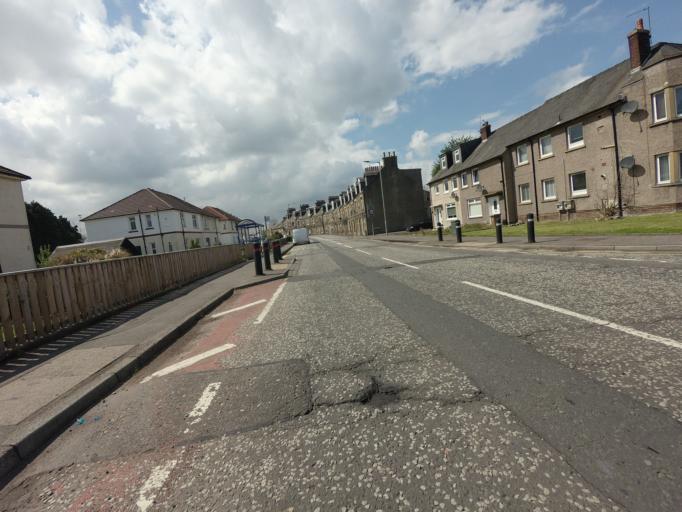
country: GB
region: Scotland
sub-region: Falkirk
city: Falkirk
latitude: 56.0258
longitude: -3.7915
